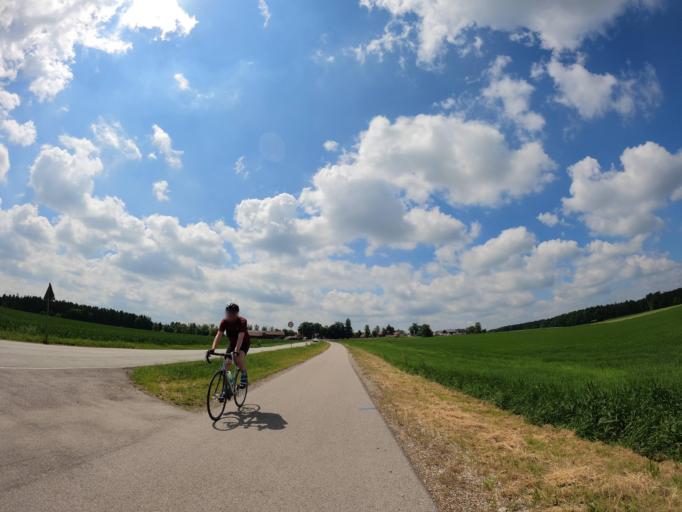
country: DE
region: Bavaria
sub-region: Upper Bavaria
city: Oberhaching
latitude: 47.9846
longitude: 11.5718
